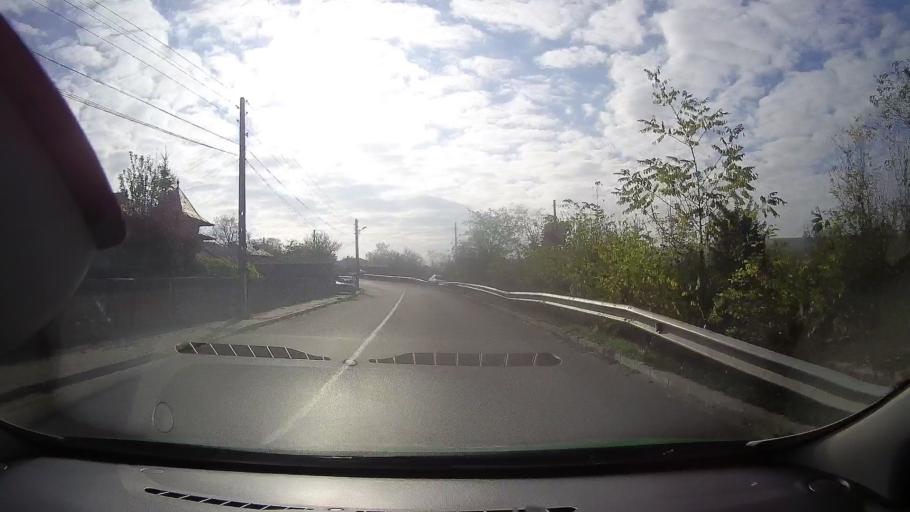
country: RO
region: Tulcea
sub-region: Comuna Bestepe
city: Bestepe
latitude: 45.0862
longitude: 29.0190
